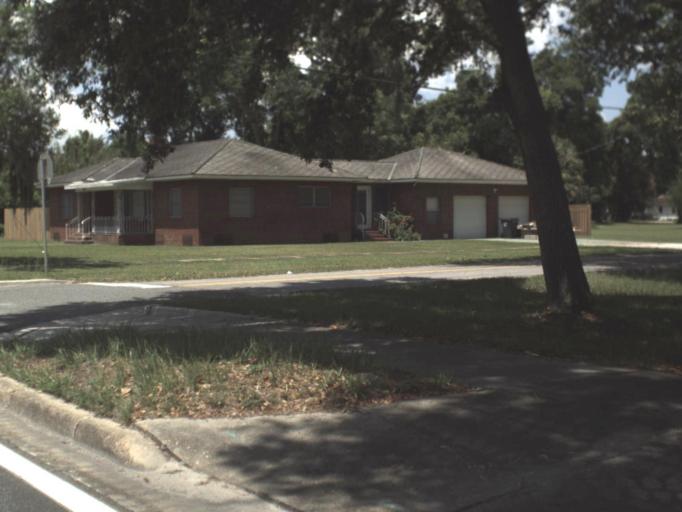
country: US
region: Florida
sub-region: Baker County
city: Macclenny
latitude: 30.2789
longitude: -82.1230
